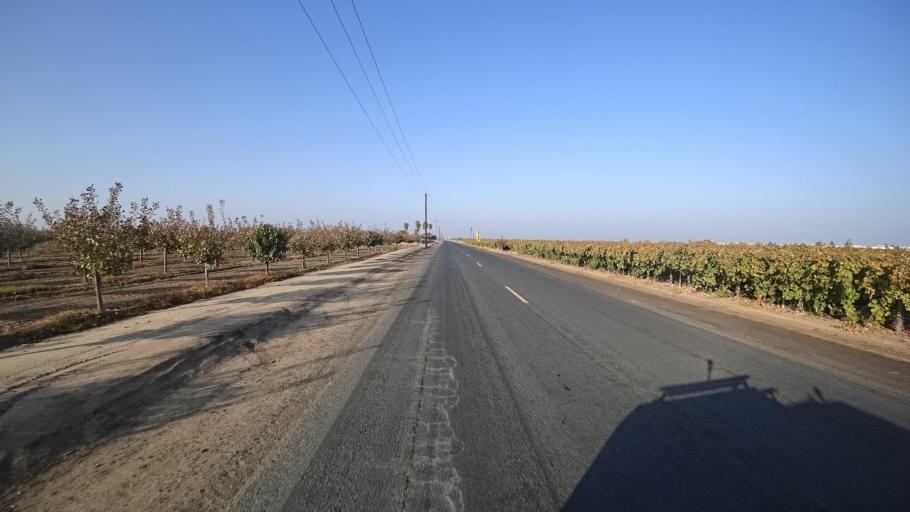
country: US
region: California
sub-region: Tulare County
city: Richgrove
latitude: 35.7906
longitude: -119.1402
